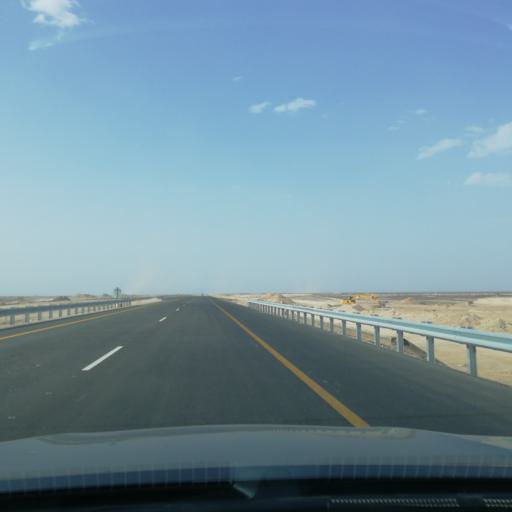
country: OM
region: Muhafazat ad Dakhiliyah
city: Adam
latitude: 22.0957
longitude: 57.5190
